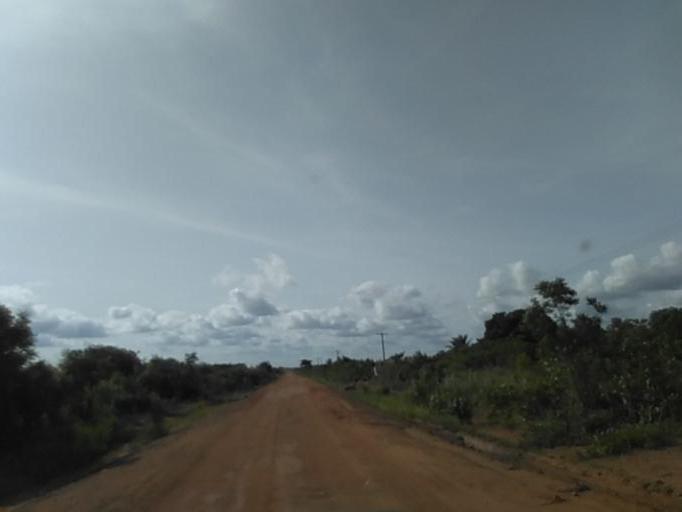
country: GH
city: Akropong
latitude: 6.0673
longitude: 0.2853
